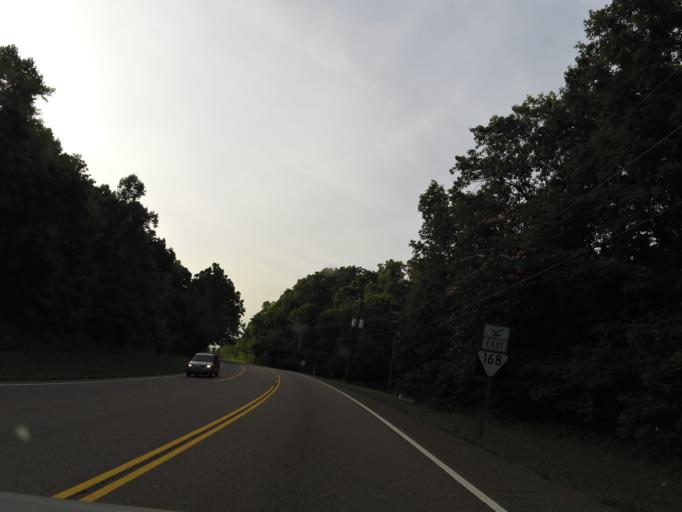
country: US
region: Tennessee
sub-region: Sevier County
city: Seymour
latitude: 35.9296
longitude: -83.8102
